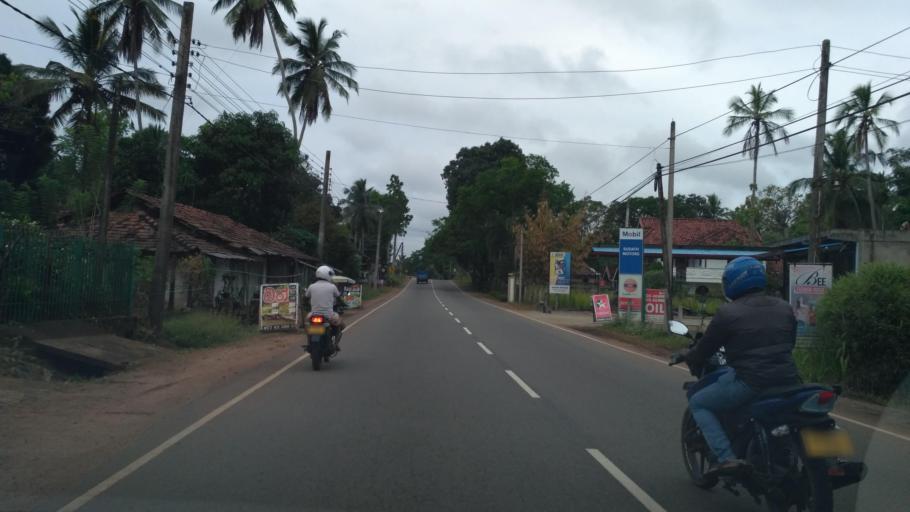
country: LK
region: North Western
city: Kuliyapitiya
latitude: 7.3272
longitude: 80.0499
